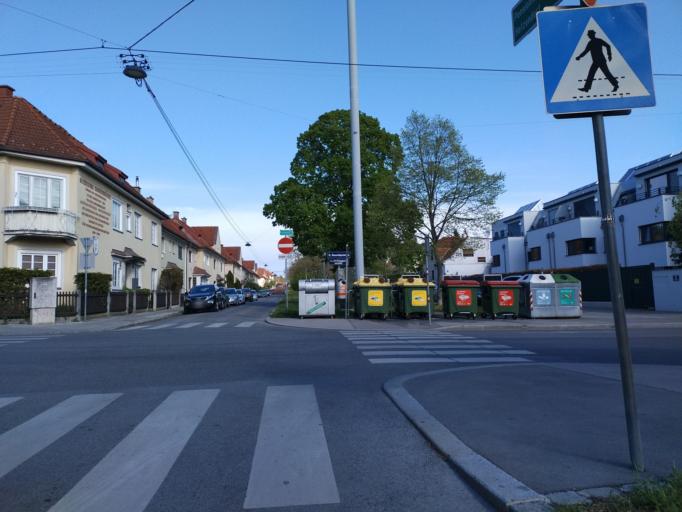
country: AT
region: Lower Austria
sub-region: Politischer Bezirk Modling
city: Perchtoldsdorf
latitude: 48.1667
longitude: 16.3002
